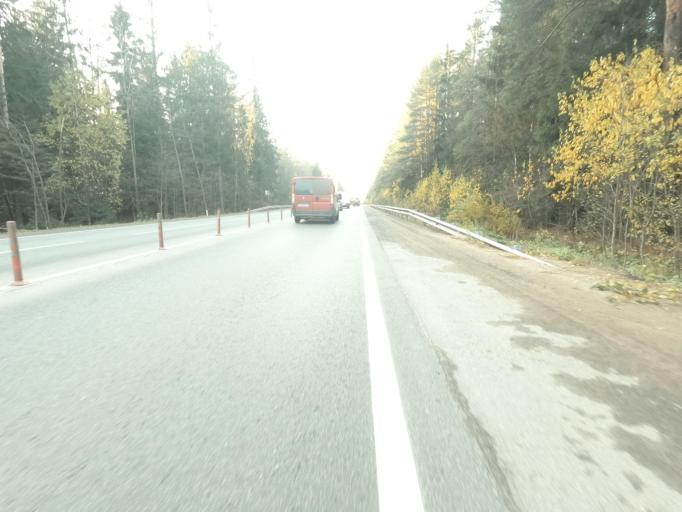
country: RU
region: St.-Petersburg
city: Pesochnyy
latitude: 60.1828
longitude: 30.1267
